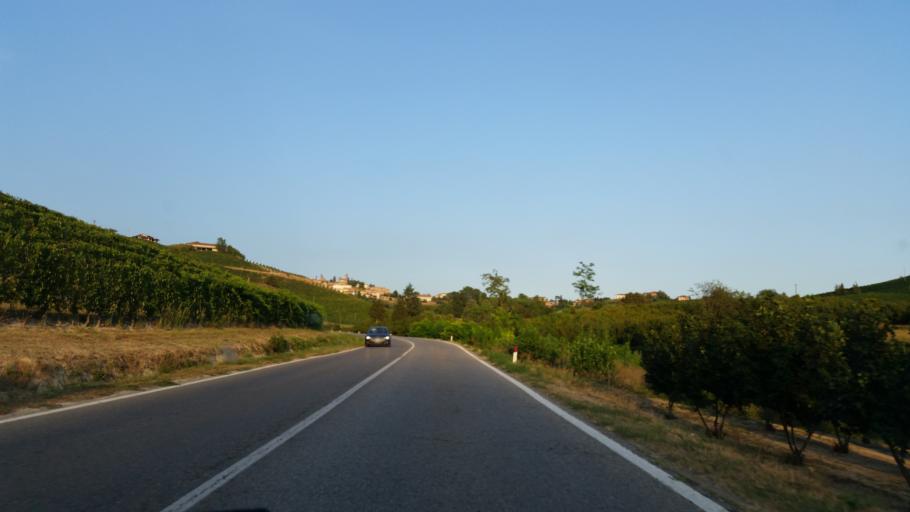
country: IT
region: Piedmont
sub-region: Provincia di Cuneo
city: Barbaresco
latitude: 44.7282
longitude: 8.0957
